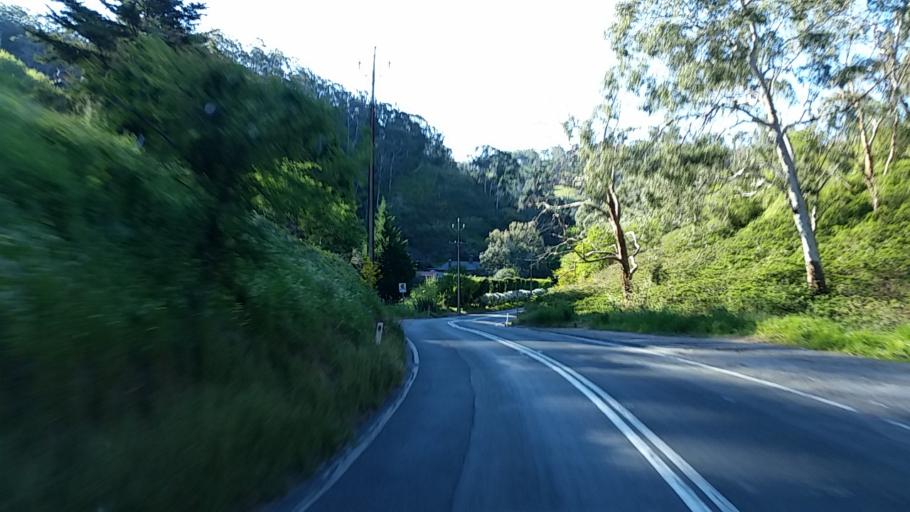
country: AU
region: South Australia
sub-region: Adelaide Hills
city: Adelaide Hills
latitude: -34.9265
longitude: 138.7186
